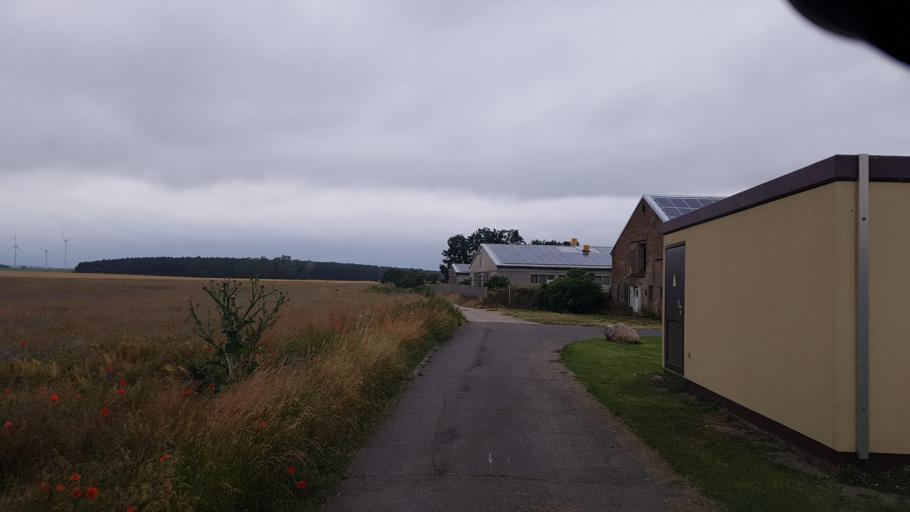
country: DE
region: Brandenburg
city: Juterbog
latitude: 51.9340
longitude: 13.2040
